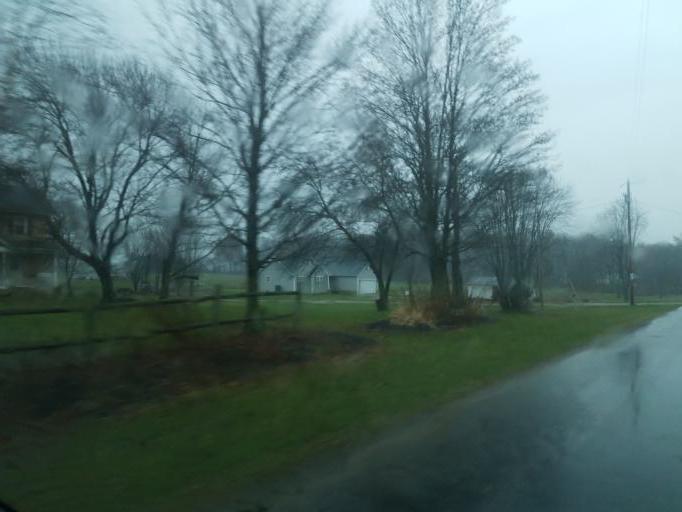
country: US
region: Ohio
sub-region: Morrow County
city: Cardington
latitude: 40.4443
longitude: -82.8722
